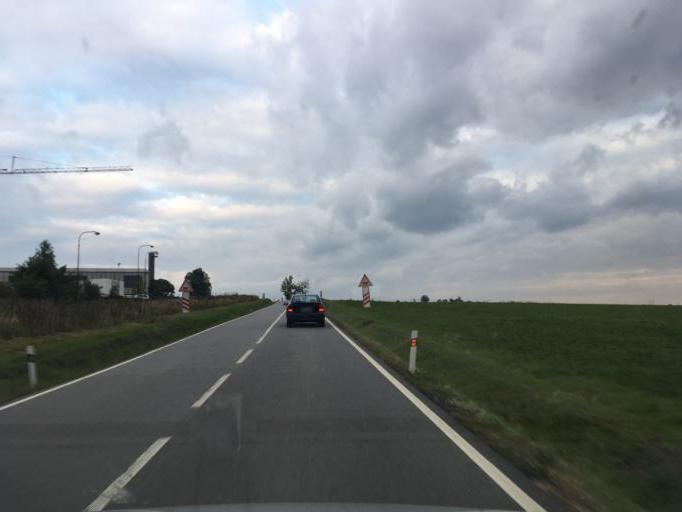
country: CZ
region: Vysocina
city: Starec
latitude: 49.2113
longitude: 15.8095
